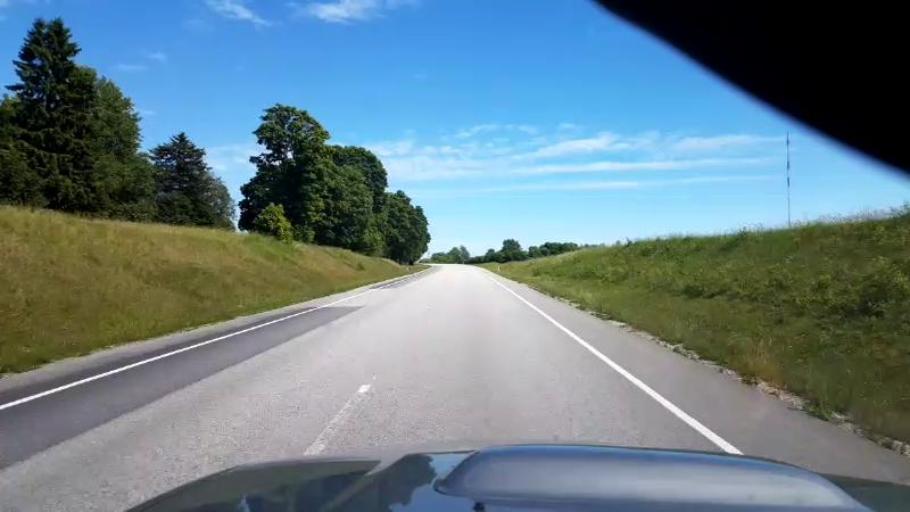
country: EE
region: Jaervamaa
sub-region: Koeru vald
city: Koeru
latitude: 58.9852
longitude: 26.0275
